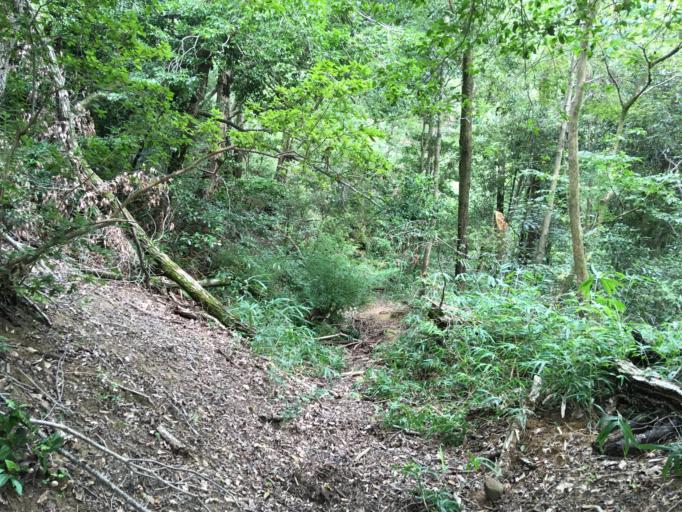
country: JP
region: Nara
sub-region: Ikoma-shi
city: Ikoma
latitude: 34.6992
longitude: 135.6638
